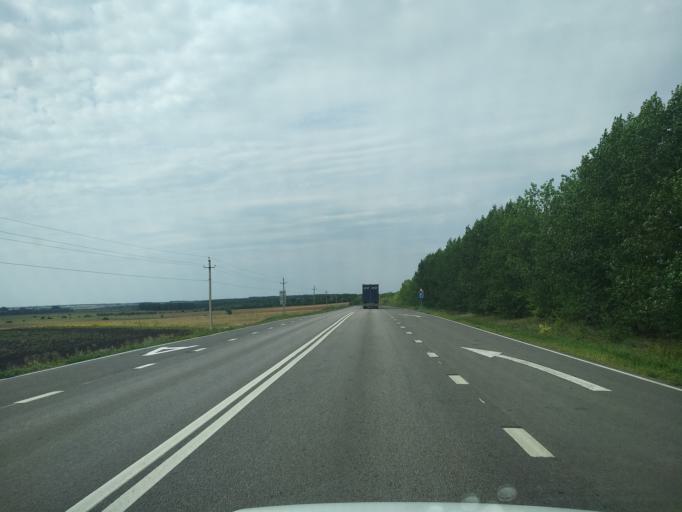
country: RU
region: Voronezj
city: Pereleshinskiy
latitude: 51.8395
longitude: 40.3005
